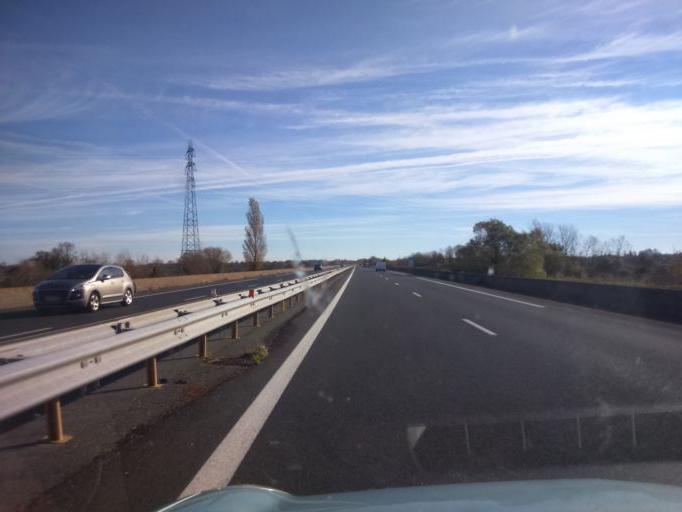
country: FR
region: Poitou-Charentes
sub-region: Departement de la Charente-Maritime
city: Tonnay-Charente
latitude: 45.9575
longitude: -0.9316
